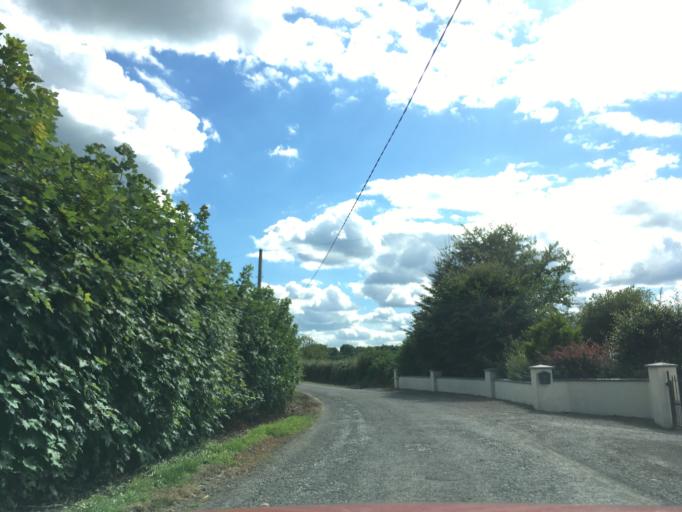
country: IE
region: Munster
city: Cashel
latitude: 52.4933
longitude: -7.9334
